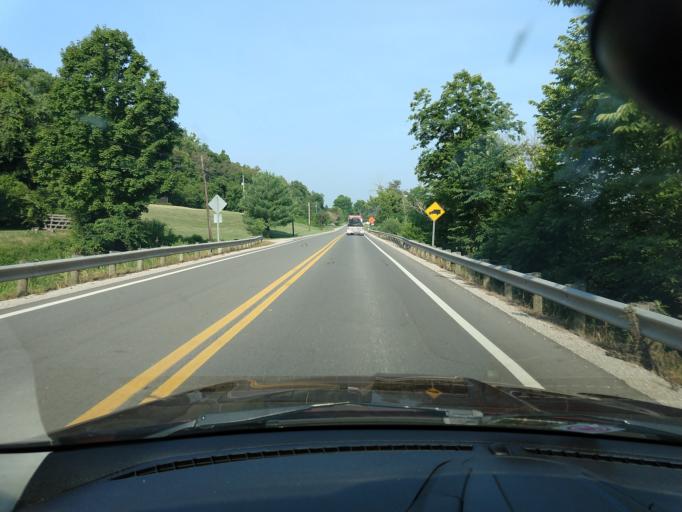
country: US
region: West Virginia
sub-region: Jackson County
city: Ravenswood
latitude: 38.8831
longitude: -81.8502
